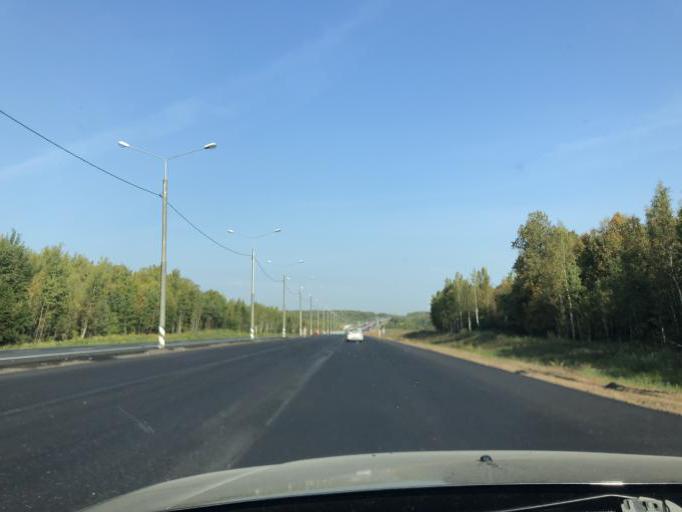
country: RU
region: Tula
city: Zaokskiy
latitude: 54.5759
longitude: 37.5079
